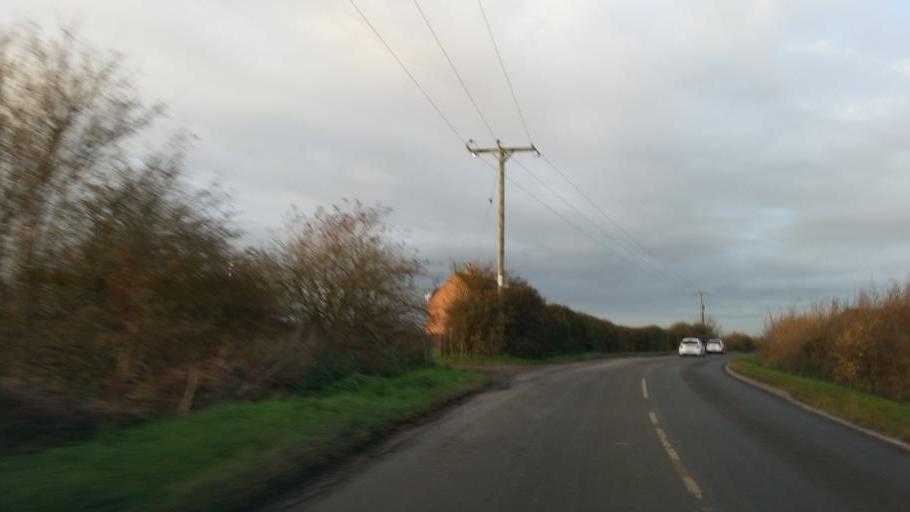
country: GB
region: England
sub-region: Nottinghamshire
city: Newark on Trent
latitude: 53.0289
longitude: -0.8017
